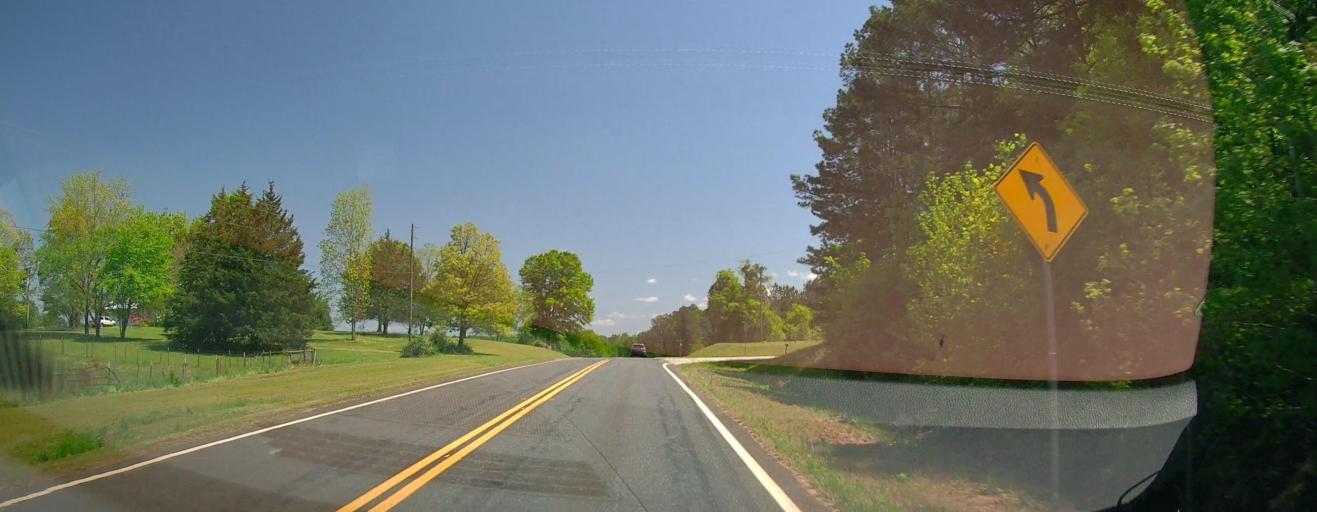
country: US
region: Georgia
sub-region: Jasper County
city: Monticello
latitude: 33.2675
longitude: -83.5848
